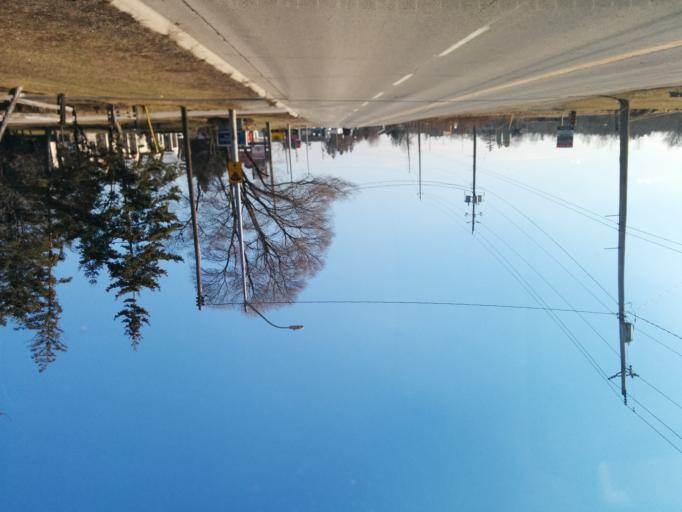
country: CA
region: Ontario
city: Norfolk County
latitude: 42.8437
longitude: -80.3207
